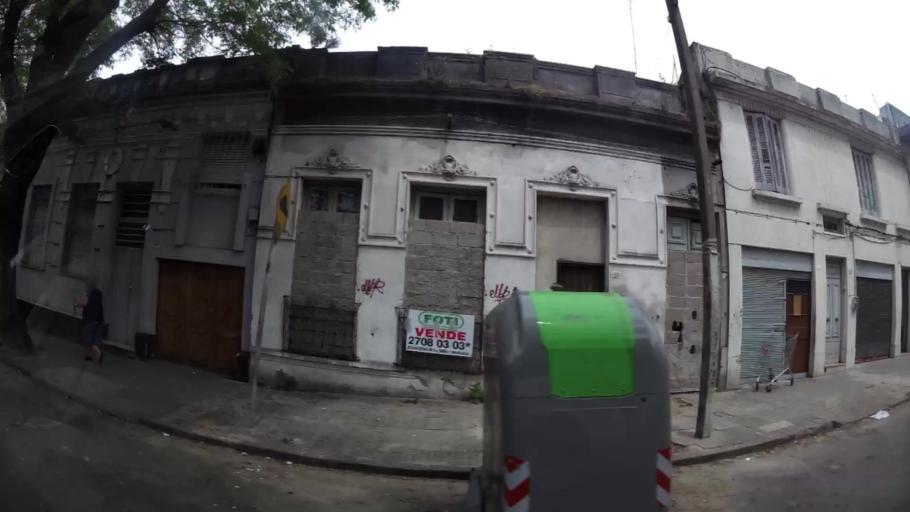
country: UY
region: Montevideo
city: Montevideo
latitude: -34.8948
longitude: -56.1730
